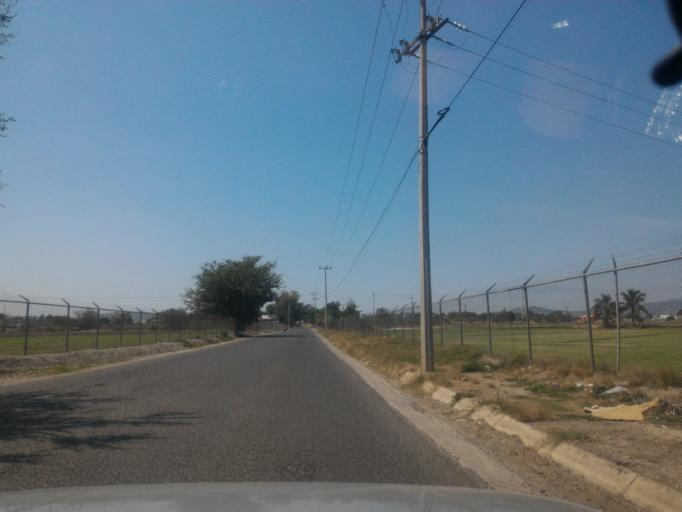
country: MX
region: Jalisco
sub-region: San Pedro Tlaquepaque
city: Santa Anita
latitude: 20.5582
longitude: -103.4225
